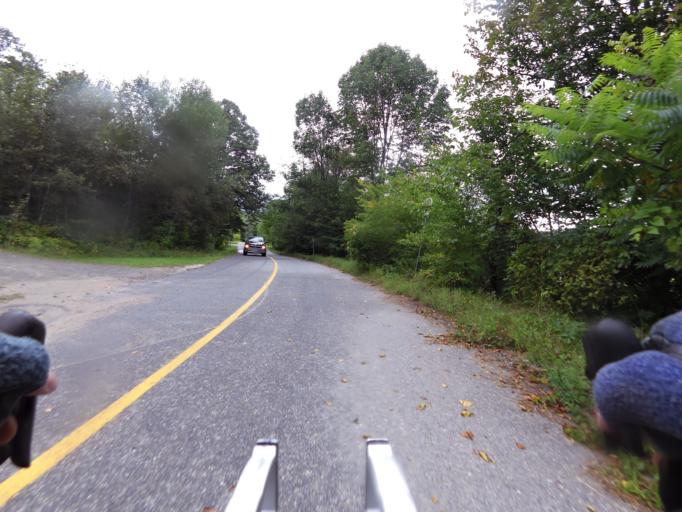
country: CA
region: Quebec
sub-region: Outaouais
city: Wakefield
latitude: 45.6471
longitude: -75.9230
